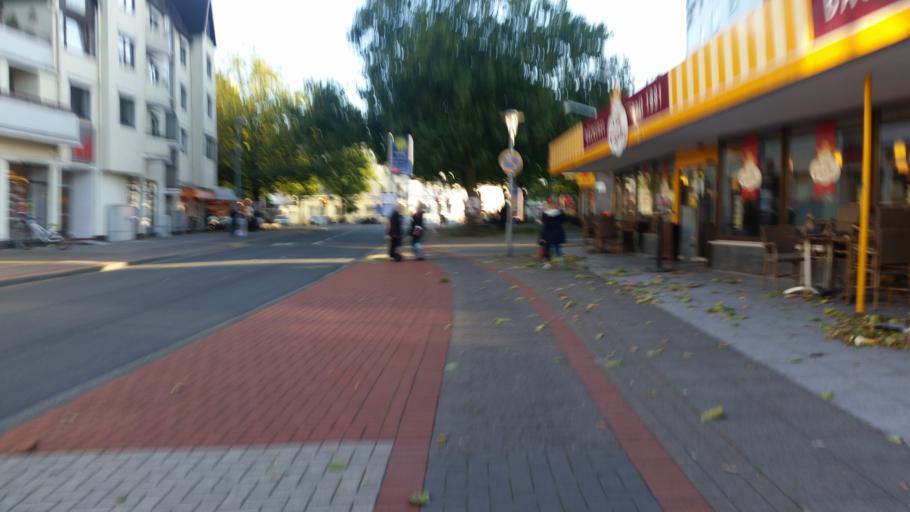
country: DE
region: Lower Saxony
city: Isernhagen Farster Bauerschaft
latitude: 52.3913
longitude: 9.8540
